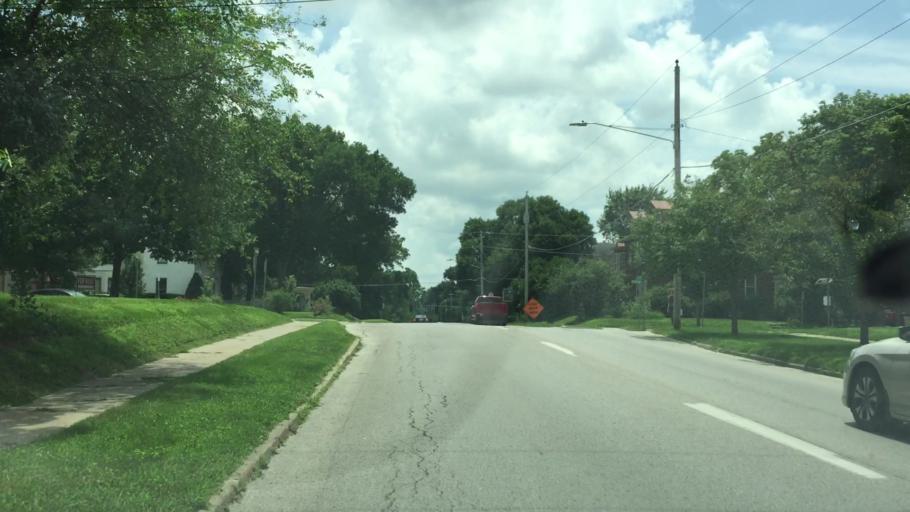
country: US
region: Iowa
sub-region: Johnson County
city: Iowa City
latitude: 41.6593
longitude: -91.5258
